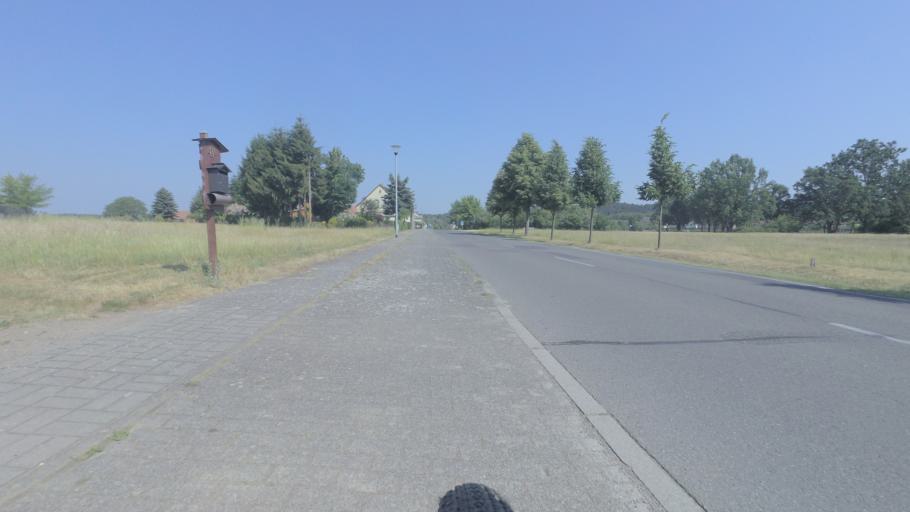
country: DE
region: Brandenburg
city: Belzig
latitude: 52.0399
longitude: 12.5761
